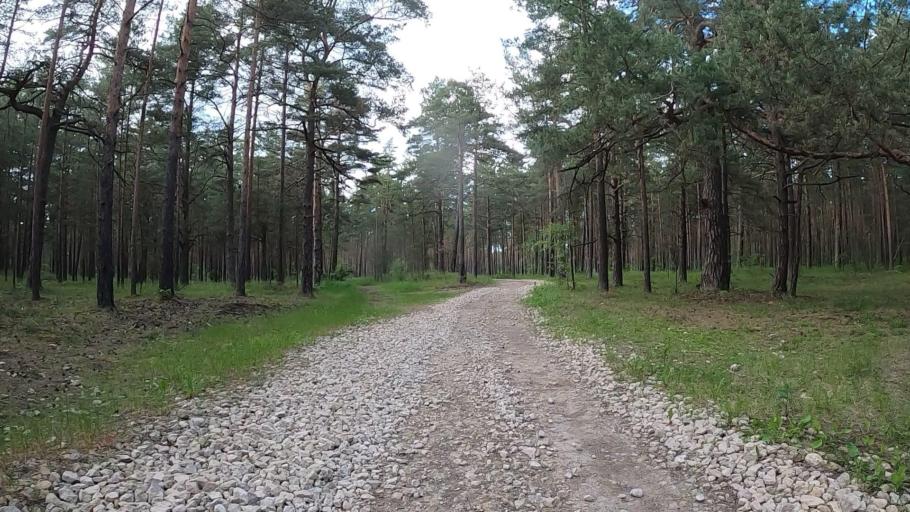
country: LV
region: Riga
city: Jaunciems
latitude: 57.0468
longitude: 24.1151
